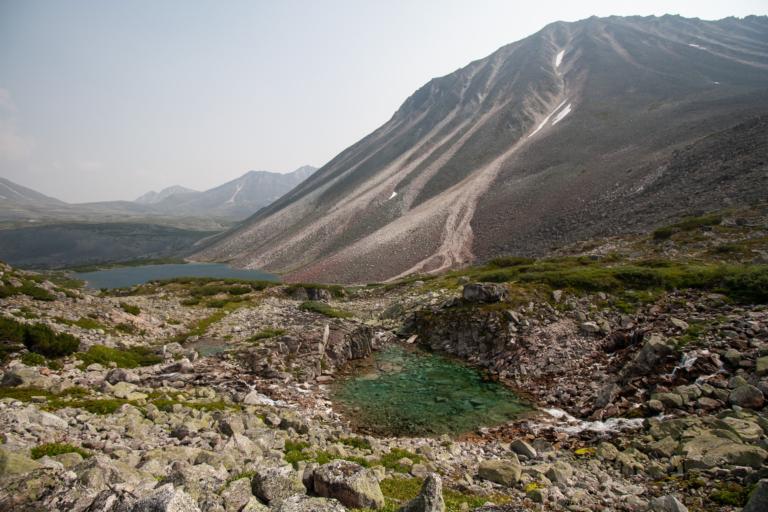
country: RU
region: Respublika Buryatiya
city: Novyy Uoyan
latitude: 56.2137
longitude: 111.0368
